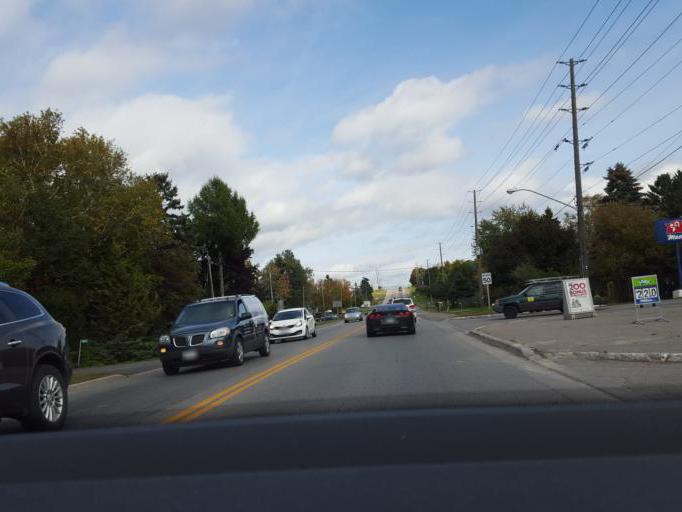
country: CA
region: Ontario
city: Oshawa
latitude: 43.9496
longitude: -78.8054
